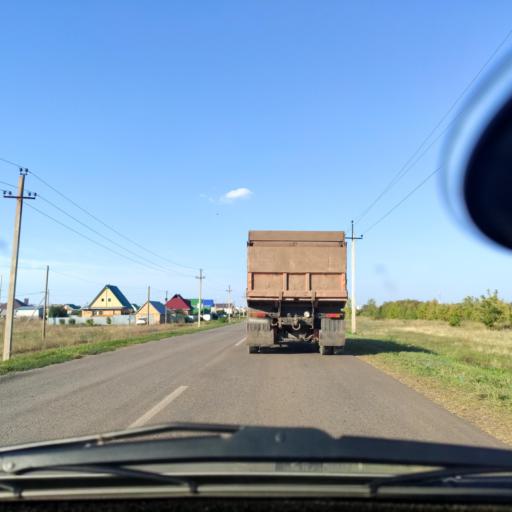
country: RU
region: Bashkortostan
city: Meleuz
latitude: 52.9397
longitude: 55.8940
